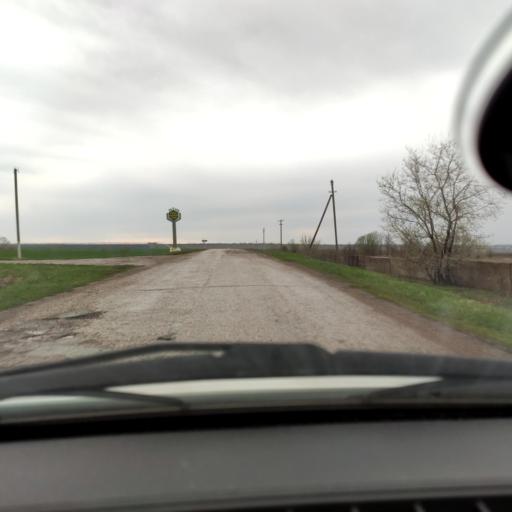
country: RU
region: Bashkortostan
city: Tolbazy
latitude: 54.1688
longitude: 55.9454
